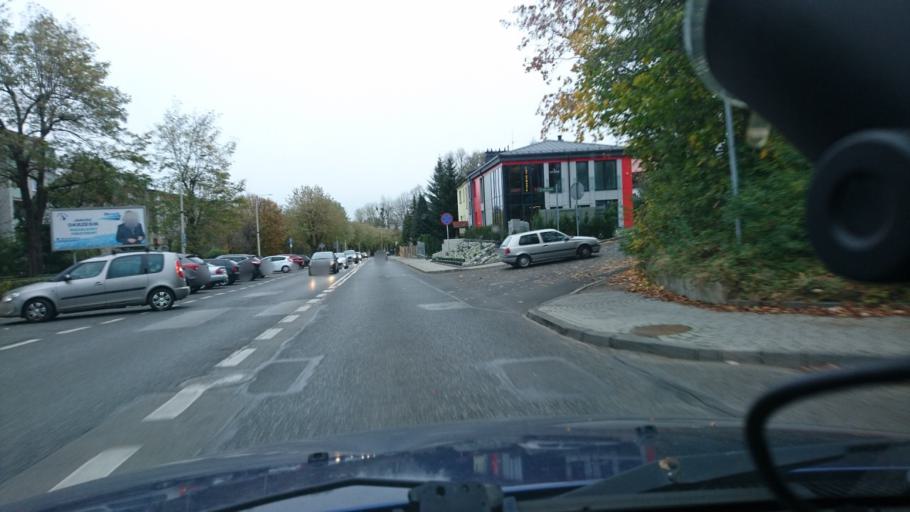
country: PL
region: Silesian Voivodeship
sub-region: Bielsko-Biala
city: Bielsko-Biala
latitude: 49.8191
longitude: 19.0223
